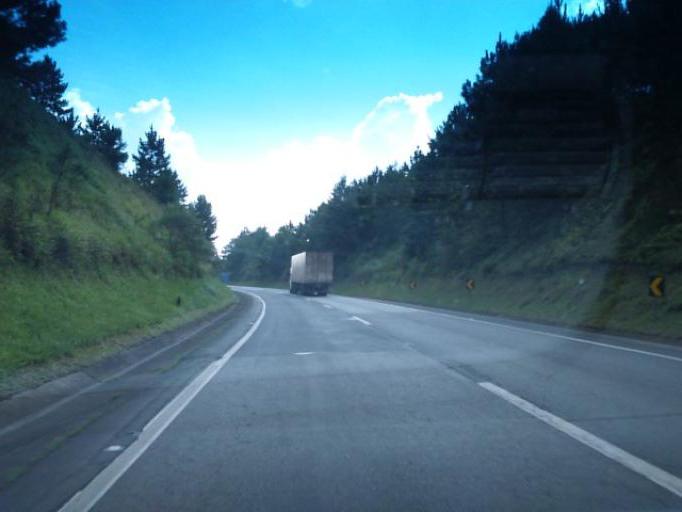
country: BR
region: Parana
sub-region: Campina Grande Do Sul
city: Campina Grande do Sul
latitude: -25.1066
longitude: -48.8490
